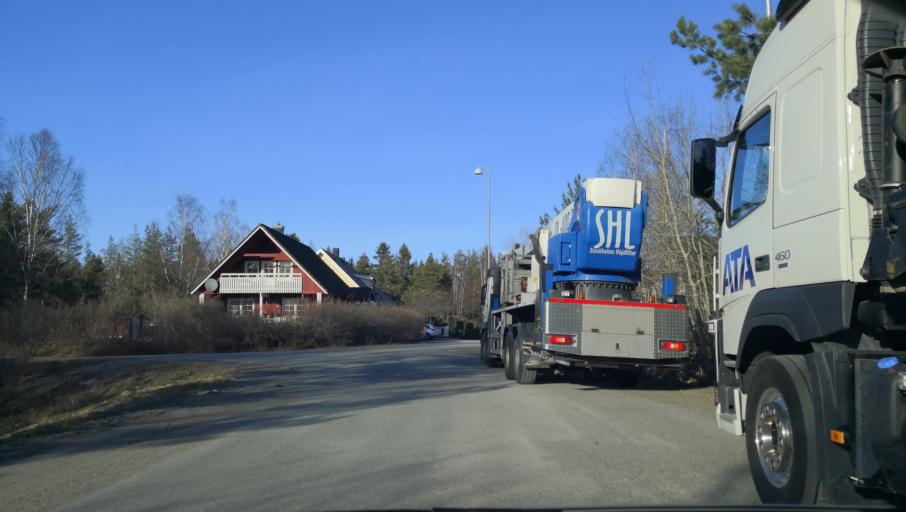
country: SE
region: Stockholm
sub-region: Varmdo Kommun
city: Gustavsberg
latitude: 59.3386
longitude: 18.3780
